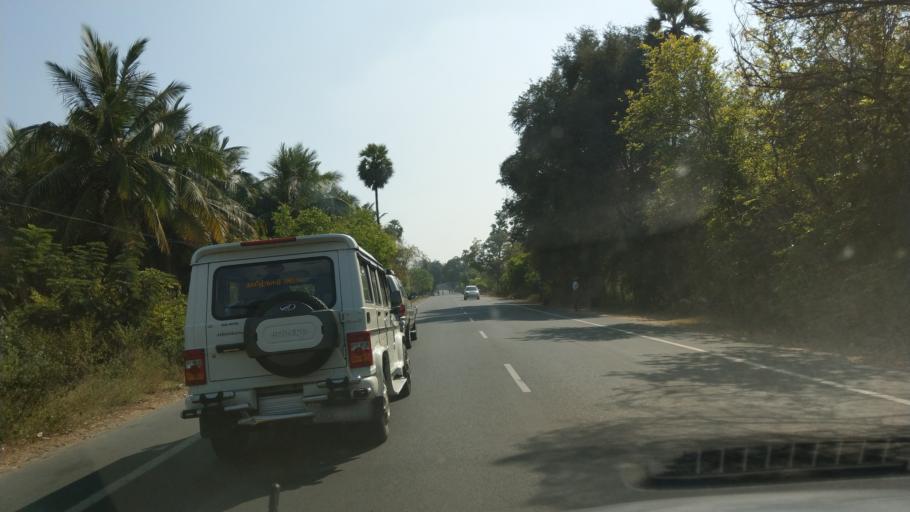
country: IN
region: Tamil Nadu
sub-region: Vellore
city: Arcot
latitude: 12.8814
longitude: 79.3168
